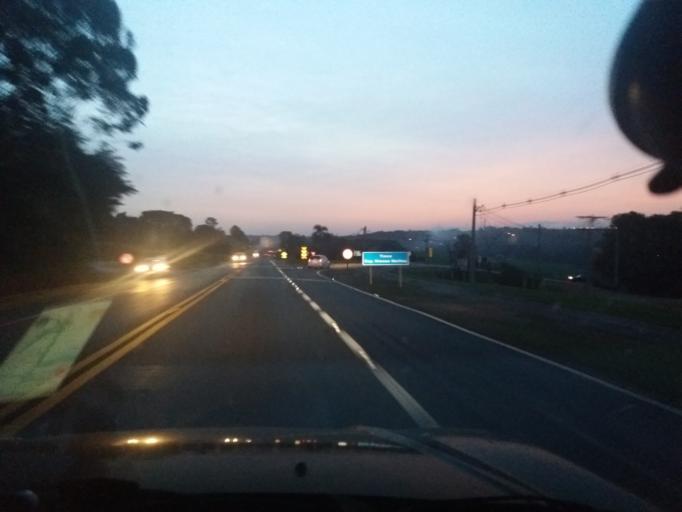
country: BR
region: Sao Paulo
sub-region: Itapeva
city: Itapeva
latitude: -23.9730
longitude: -48.8608
